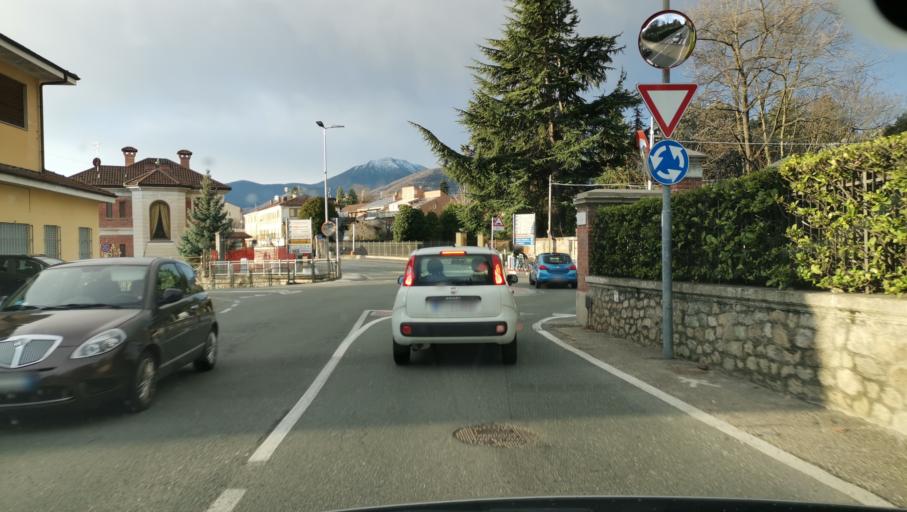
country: IT
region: Piedmont
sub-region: Provincia di Torino
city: Giaveno
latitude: 45.0469
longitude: 7.3549
